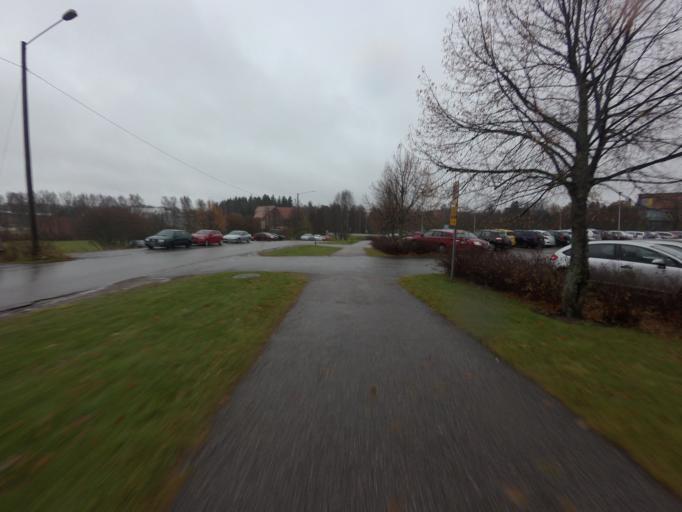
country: FI
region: Uusimaa
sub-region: Helsinki
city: Espoo
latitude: 60.2126
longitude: 24.6561
